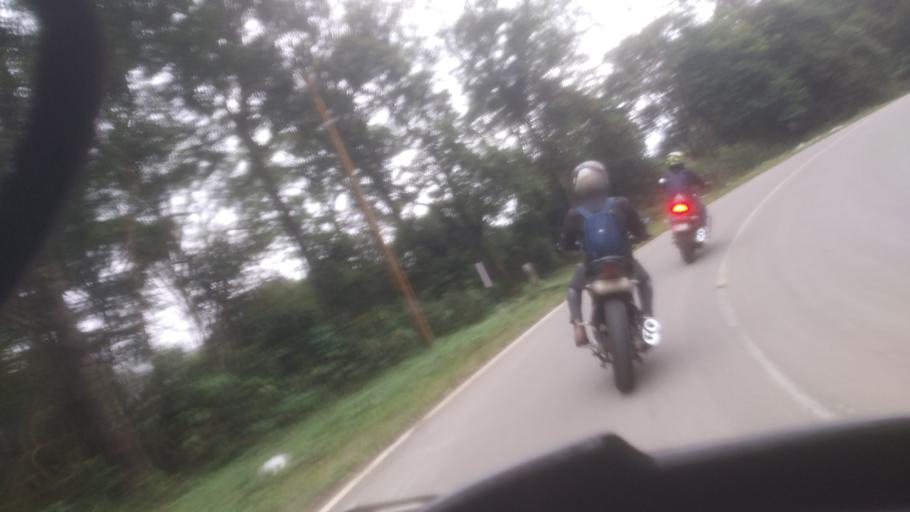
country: IN
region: Tamil Nadu
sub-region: Theni
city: Kombai
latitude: 9.8926
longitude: 77.2064
